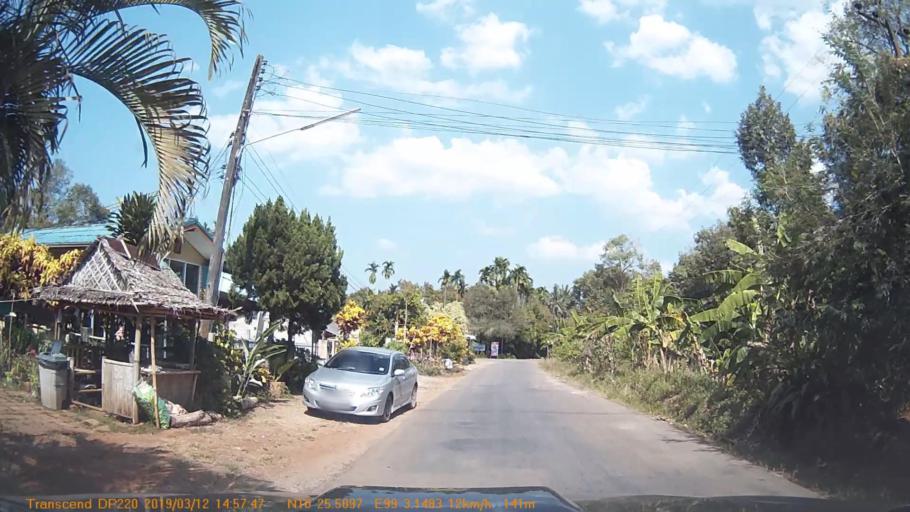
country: TH
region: Chumphon
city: Chumphon
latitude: 10.4247
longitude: 99.0530
